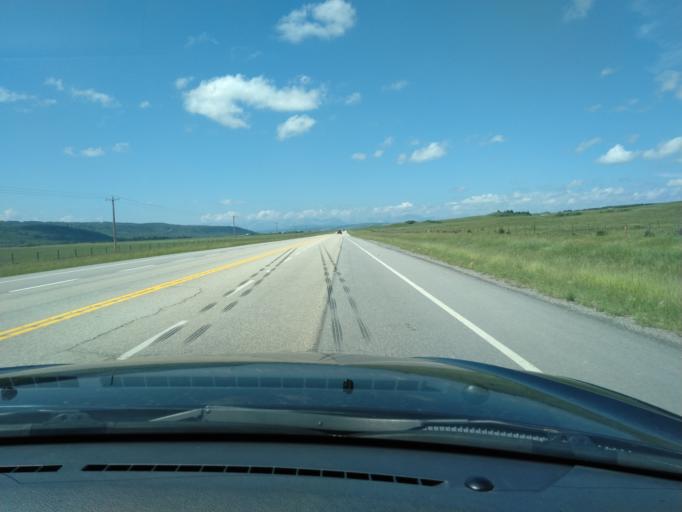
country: CA
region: Alberta
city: Cochrane
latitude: 51.2256
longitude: -114.6074
